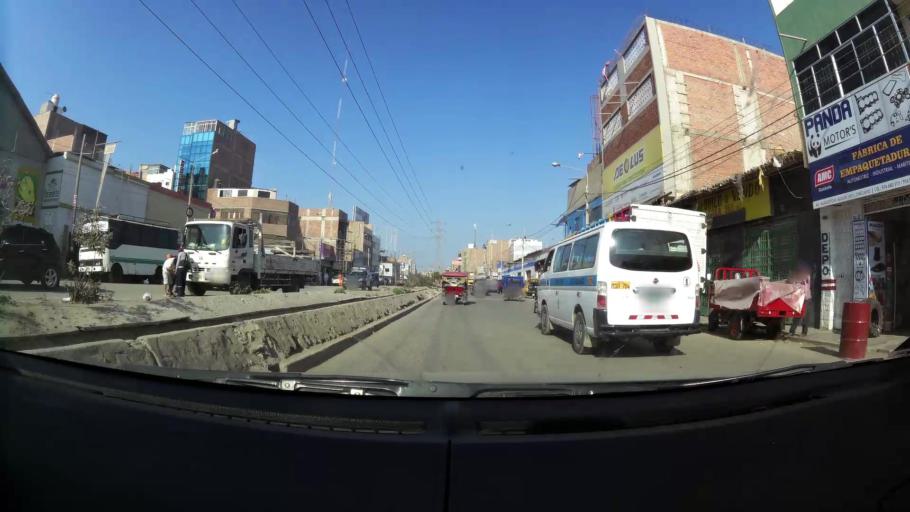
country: PE
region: Lambayeque
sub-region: Provincia de Chiclayo
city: Chiclayo
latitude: -6.7626
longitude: -79.8425
